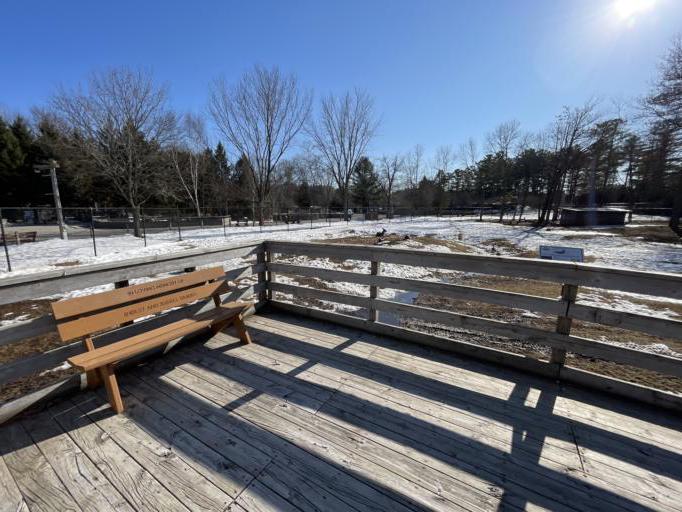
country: US
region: Wisconsin
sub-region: Brown County
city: Suamico
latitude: 44.6621
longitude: -88.0873
